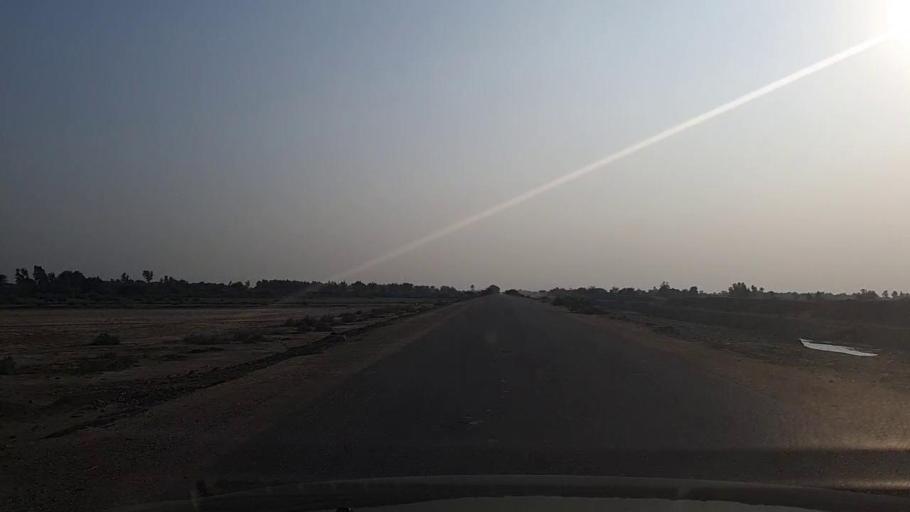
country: PK
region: Sindh
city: Mirpur Sakro
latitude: 24.5065
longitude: 67.8167
